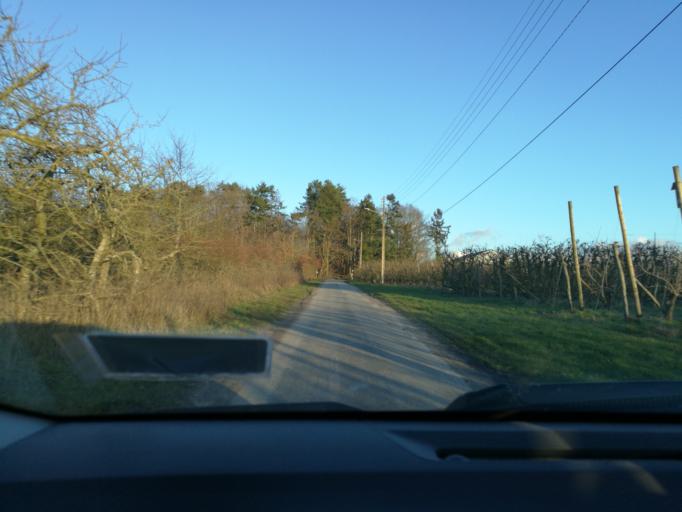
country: FR
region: Centre
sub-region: Departement du Loiret
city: Semoy
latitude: 47.9352
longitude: 1.9682
